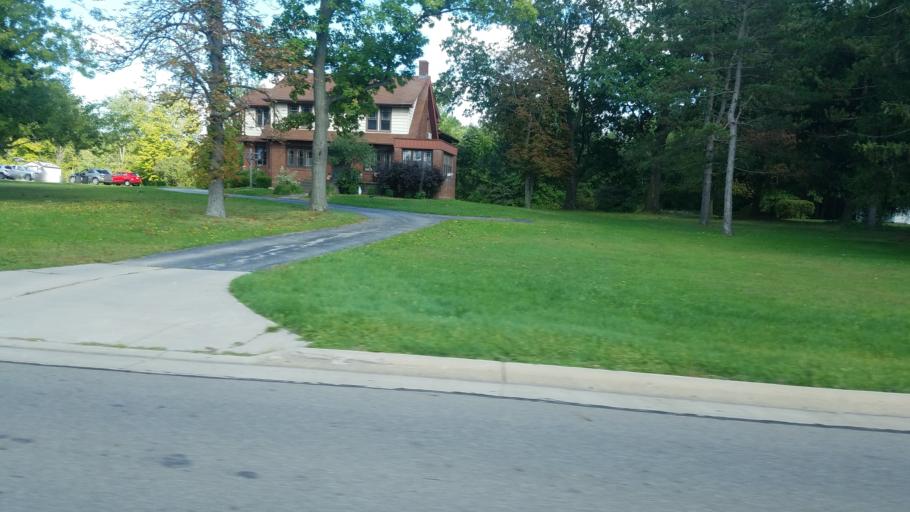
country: US
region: Ohio
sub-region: Mahoning County
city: Austintown
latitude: 41.0930
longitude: -80.7631
